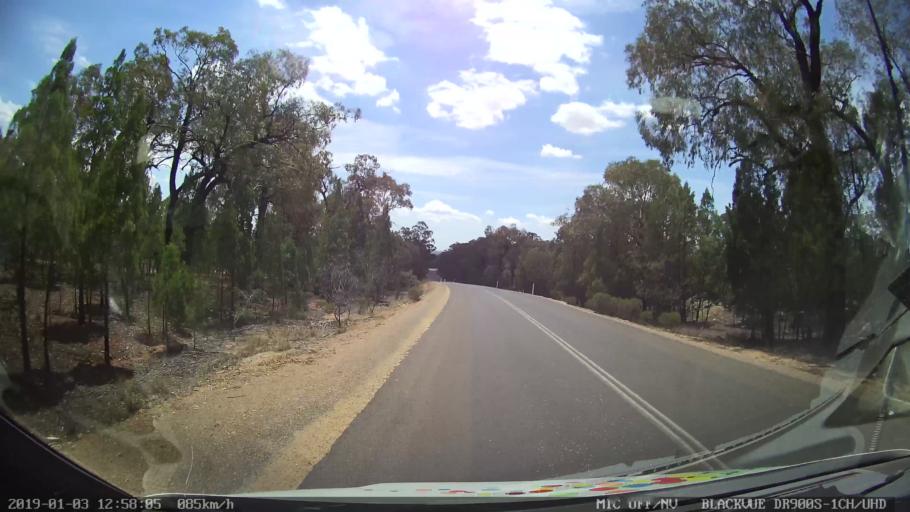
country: AU
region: New South Wales
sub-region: Cabonne
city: Canowindra
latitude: -33.6452
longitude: 148.3706
